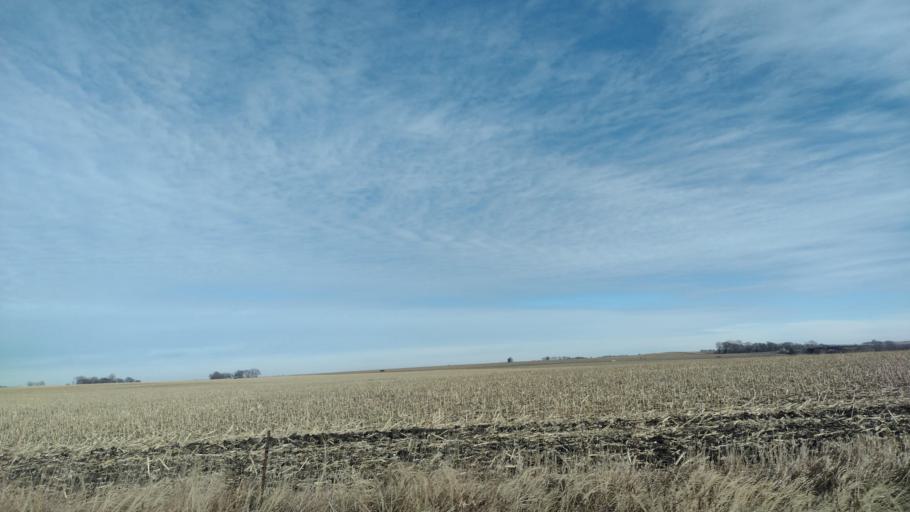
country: US
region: South Dakota
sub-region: Union County
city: Beresford
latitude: 42.9432
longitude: -96.8055
